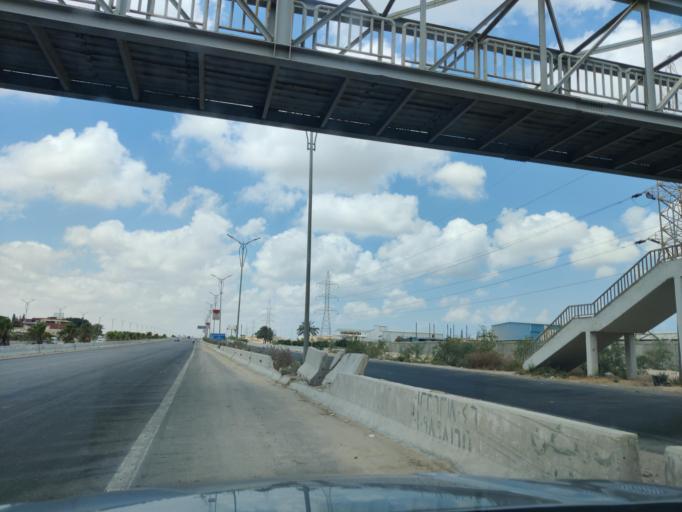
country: EG
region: Alexandria
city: Alexandria
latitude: 31.0258
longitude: 29.7746
